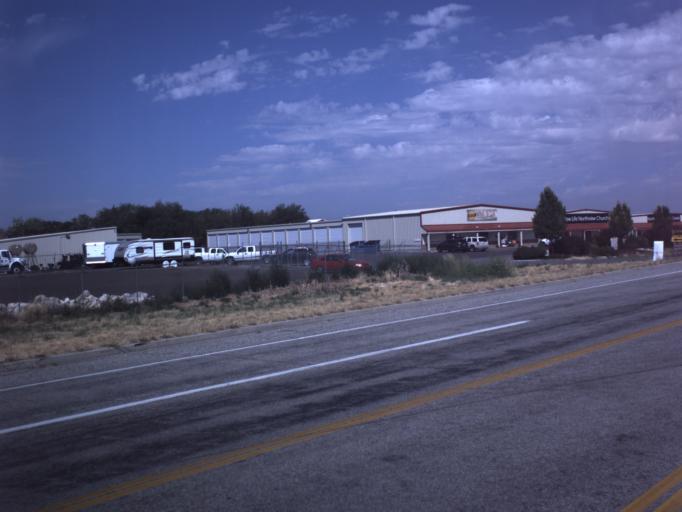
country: US
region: Utah
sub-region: Weber County
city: Farr West
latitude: 41.3215
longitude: -112.0300
